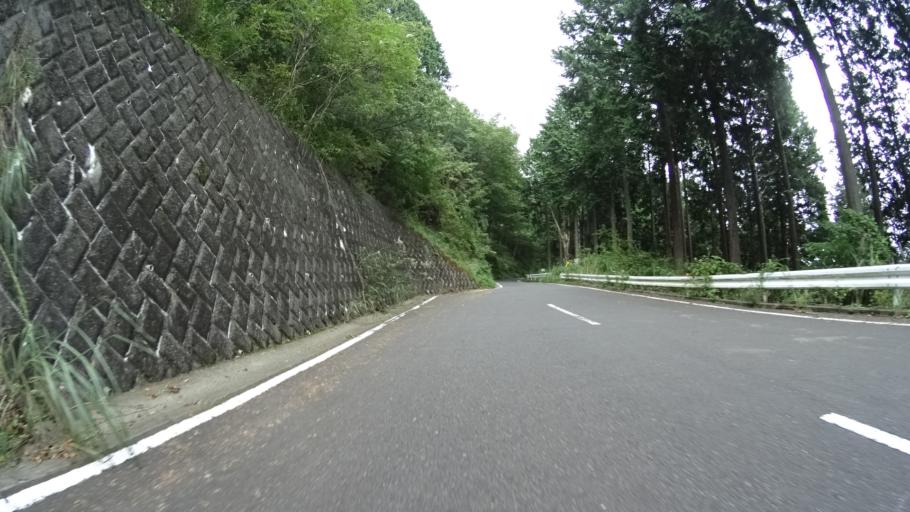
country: JP
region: Kanagawa
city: Hadano
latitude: 35.4155
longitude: 139.2138
